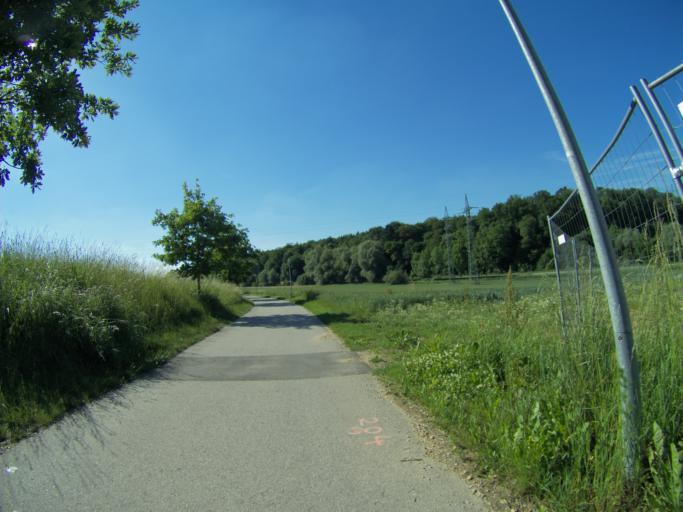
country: DE
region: Bavaria
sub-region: Upper Bavaria
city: Freising
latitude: 48.4013
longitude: 11.7139
